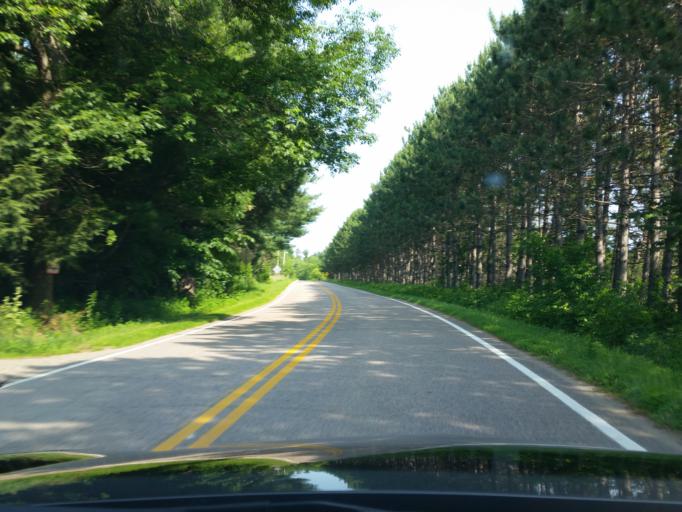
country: CA
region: Quebec
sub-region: Outaouais
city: Shawville
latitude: 45.5252
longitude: -76.4512
